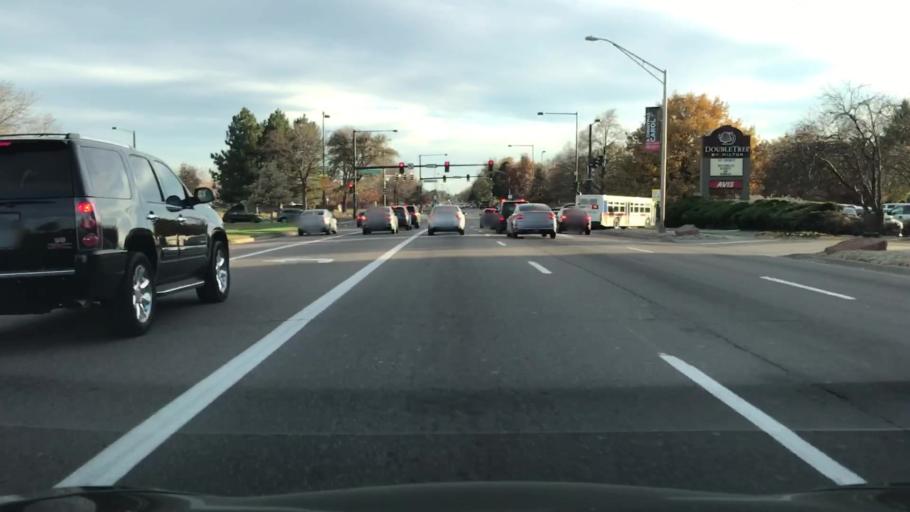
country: US
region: Colorado
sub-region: Adams County
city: Commerce City
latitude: 39.7628
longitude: -104.9034
